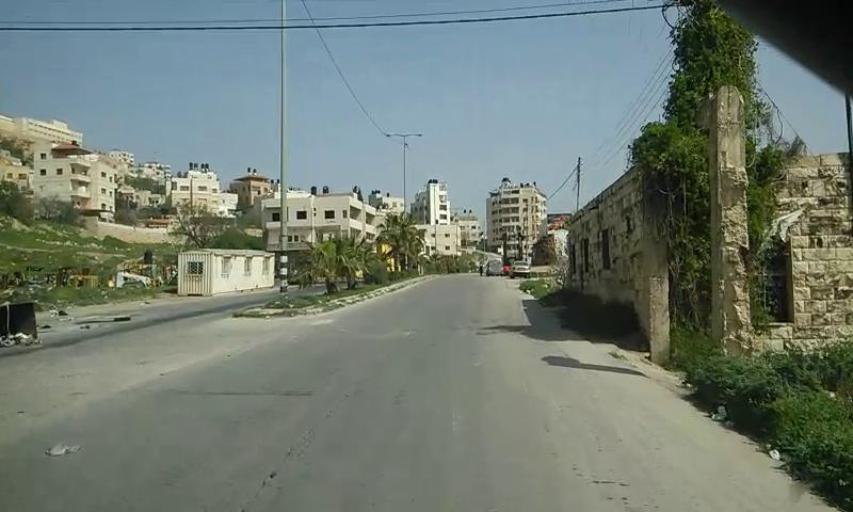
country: PS
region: West Bank
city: Balatah
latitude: 32.2157
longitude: 35.2904
